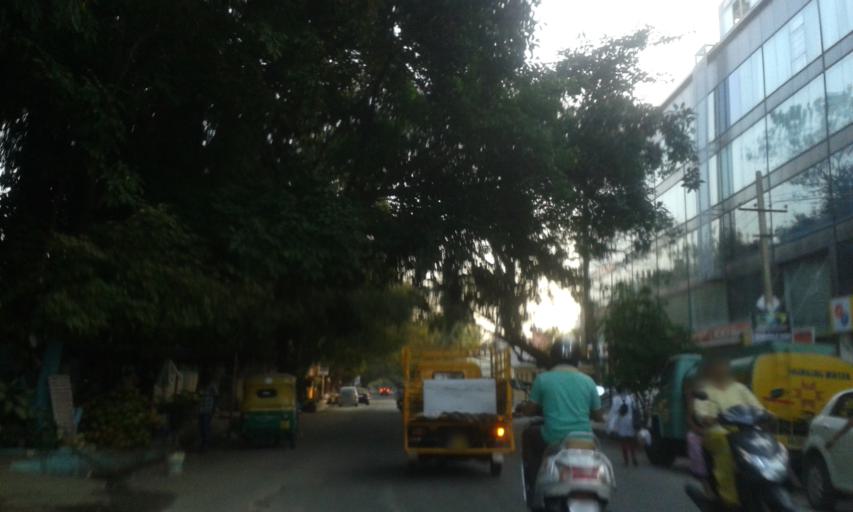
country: IN
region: Karnataka
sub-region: Bangalore Urban
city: Bangalore
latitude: 12.9144
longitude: 77.5950
